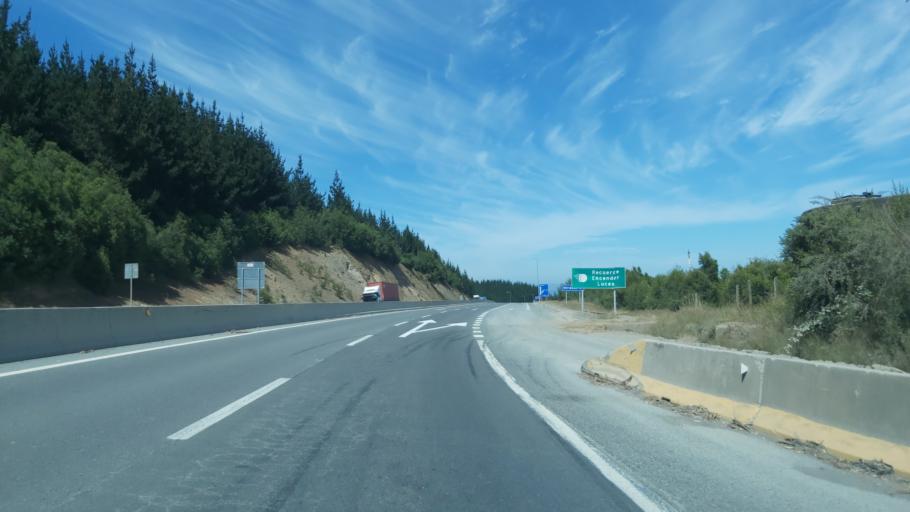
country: CL
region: Biobio
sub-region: Provincia de Concepcion
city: Lota
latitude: -37.0967
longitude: -73.1404
